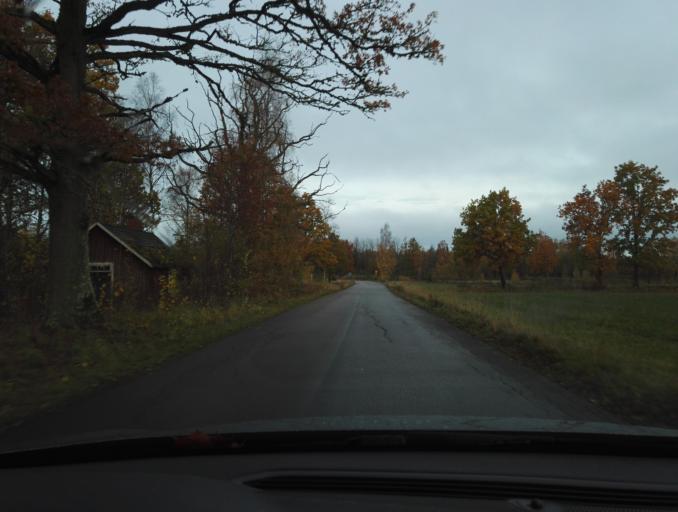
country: SE
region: Kronoberg
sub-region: Vaxjo Kommun
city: Vaexjoe
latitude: 56.9149
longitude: 14.7342
